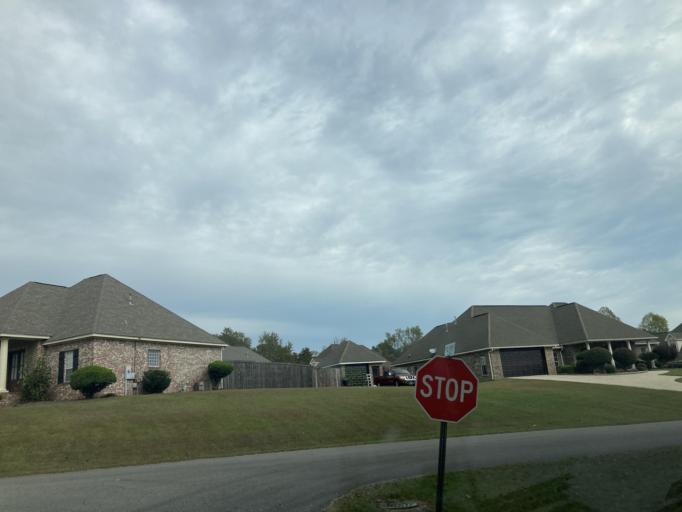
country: US
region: Mississippi
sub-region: Lamar County
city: Arnold Line
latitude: 31.3366
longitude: -89.4041
